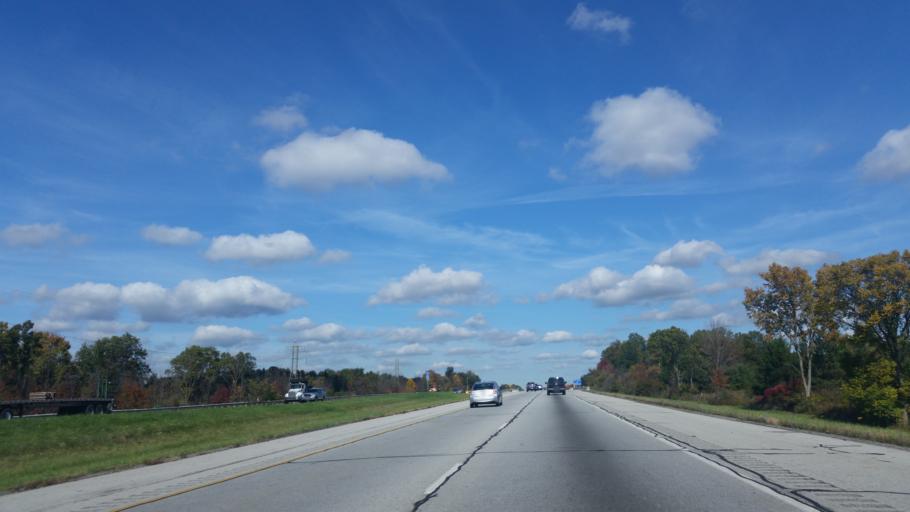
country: US
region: Ohio
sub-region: Summit County
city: Montrose-Ghent
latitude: 41.1866
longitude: -81.6255
